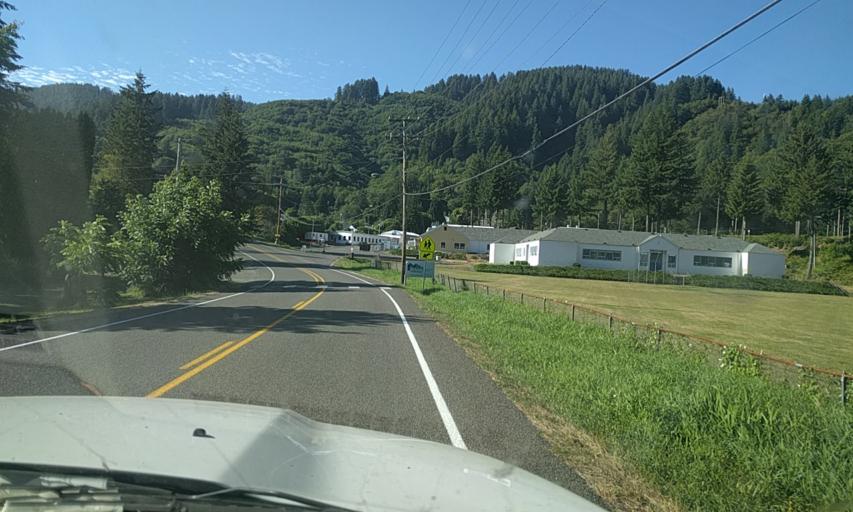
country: US
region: Oregon
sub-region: Lane County
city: Florence
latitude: 44.0343
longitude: -123.8552
